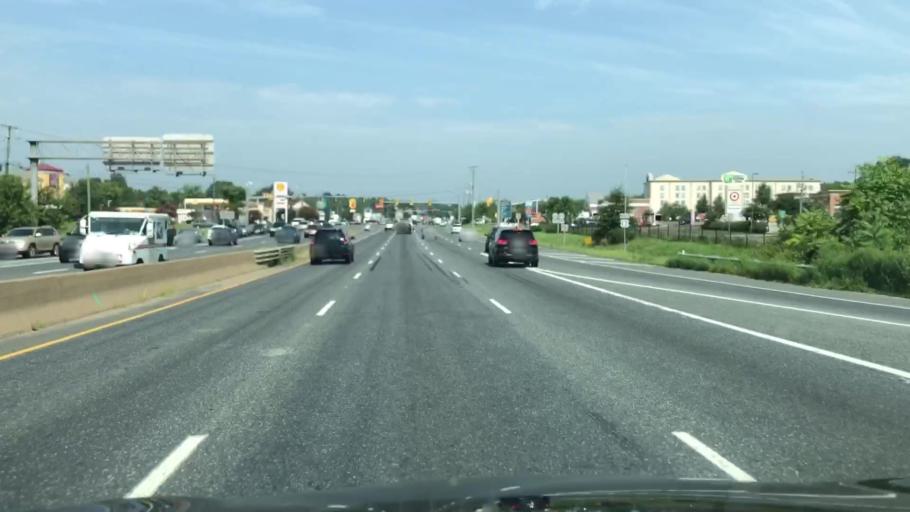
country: US
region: Virginia
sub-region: Stafford County
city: Falmouth
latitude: 38.3428
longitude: -77.4947
